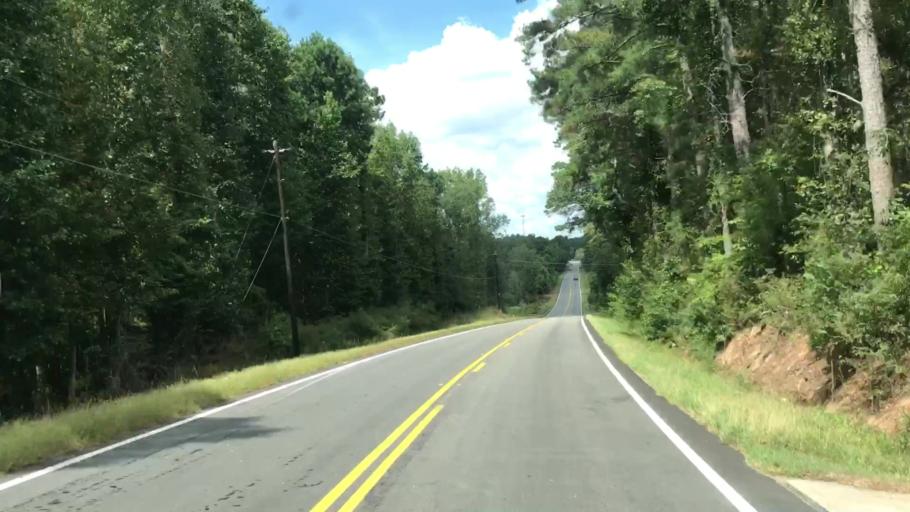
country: US
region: Georgia
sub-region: Greene County
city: Greensboro
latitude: 33.5601
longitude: -83.1376
